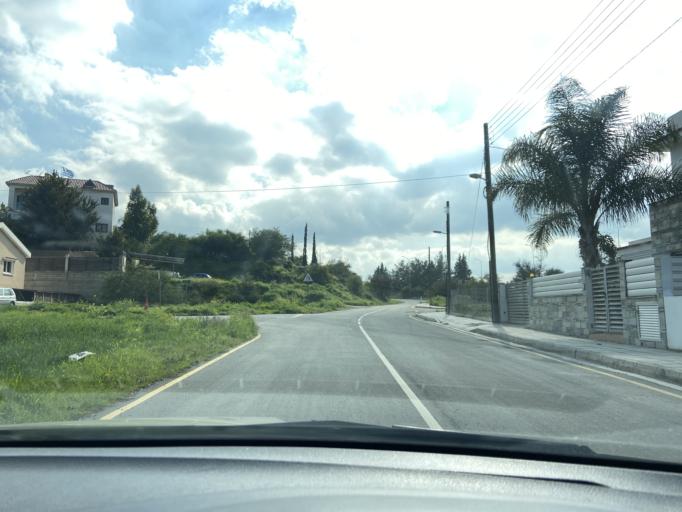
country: CY
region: Lefkosia
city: Alampra
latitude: 35.0100
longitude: 33.3866
